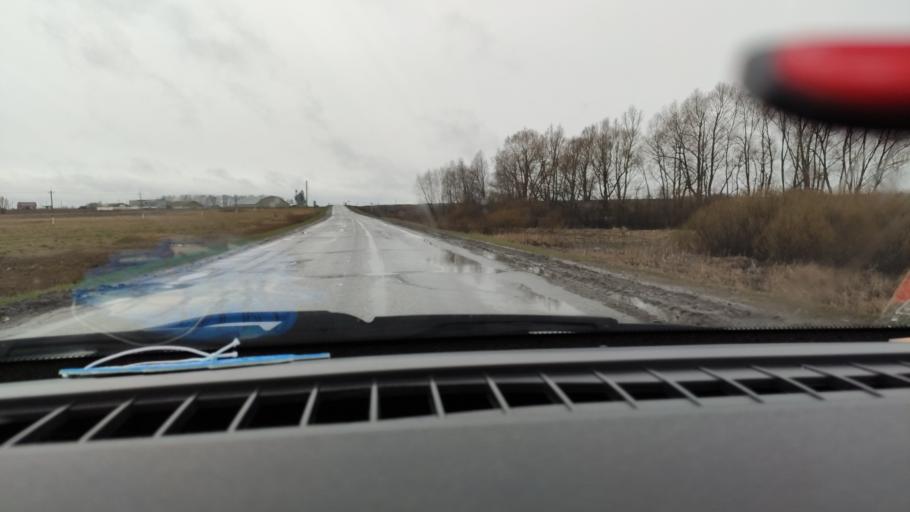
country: RU
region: Tatarstan
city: Nurlat
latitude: 54.6041
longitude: 50.8890
